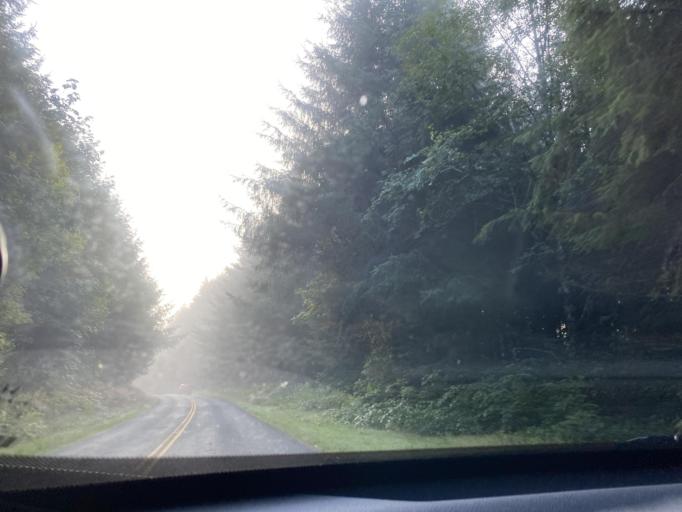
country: US
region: Washington
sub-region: Clallam County
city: Forks
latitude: 47.8097
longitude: -124.0866
